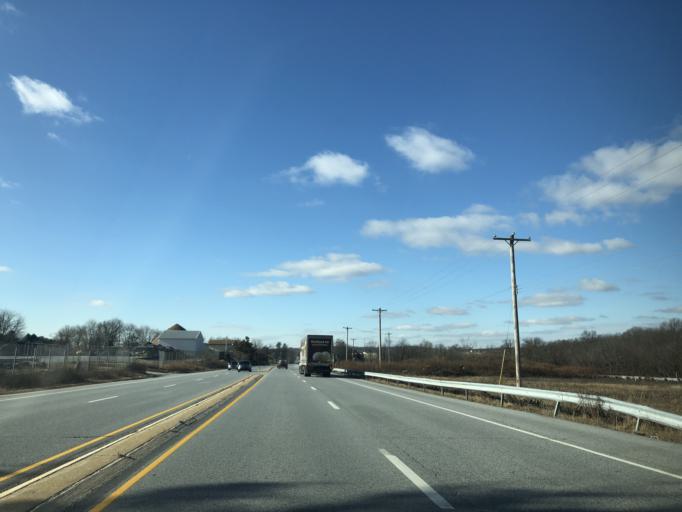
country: US
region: Pennsylvania
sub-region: Chester County
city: Parkesburg
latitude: 39.9824
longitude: -75.9197
